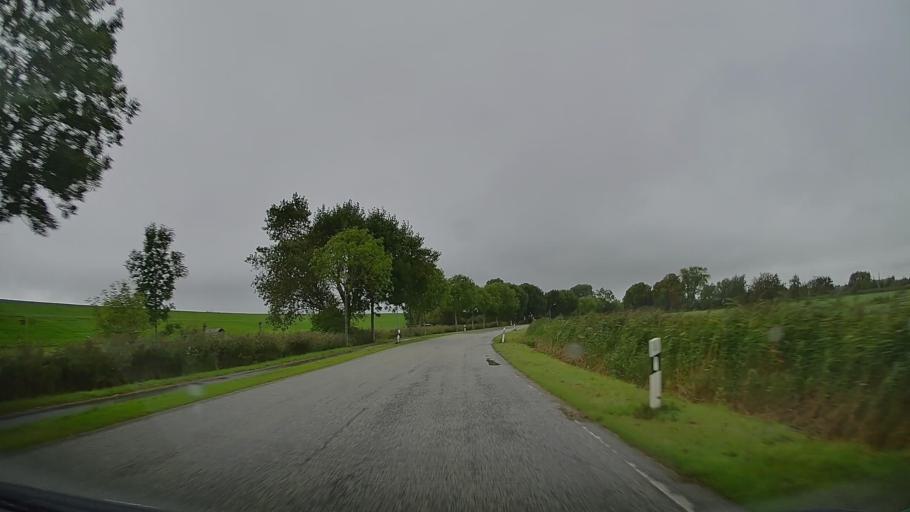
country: DE
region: Schleswig-Holstein
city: Sankt Margarethen
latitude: 53.8815
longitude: 9.2602
